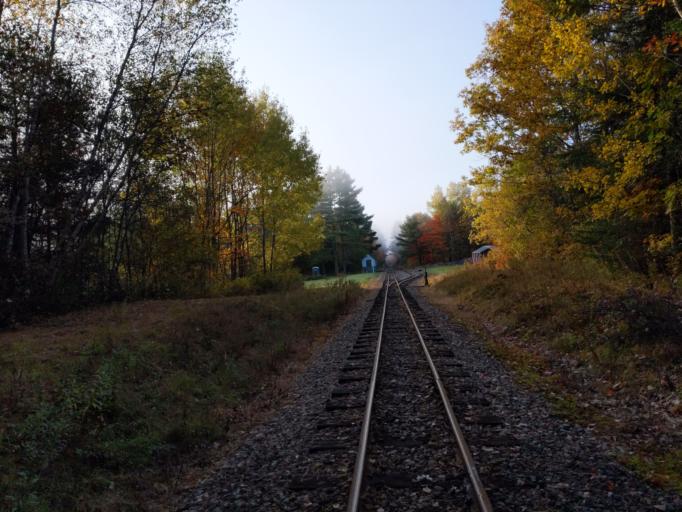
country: US
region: Maine
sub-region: Lincoln County
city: Whitefield
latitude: 44.0831
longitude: -69.6242
